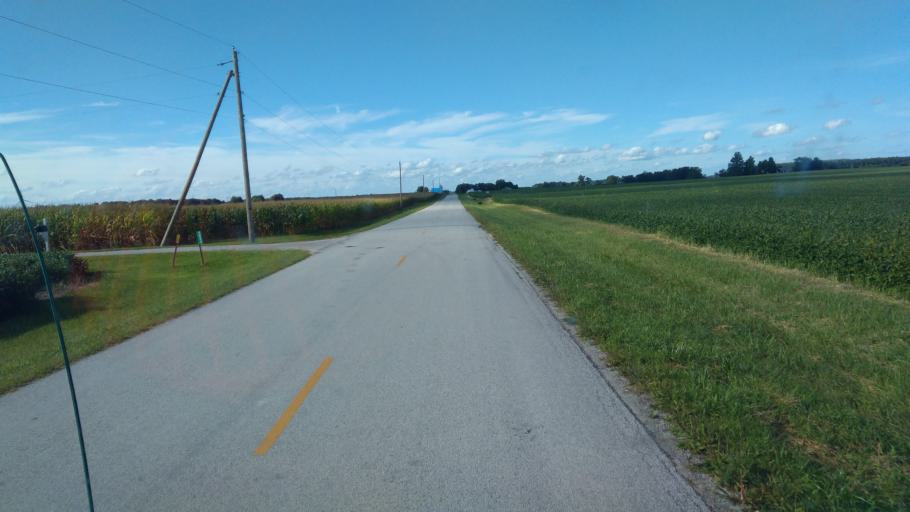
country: US
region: Ohio
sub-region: Hardin County
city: Kenton
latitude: 40.7351
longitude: -83.6907
